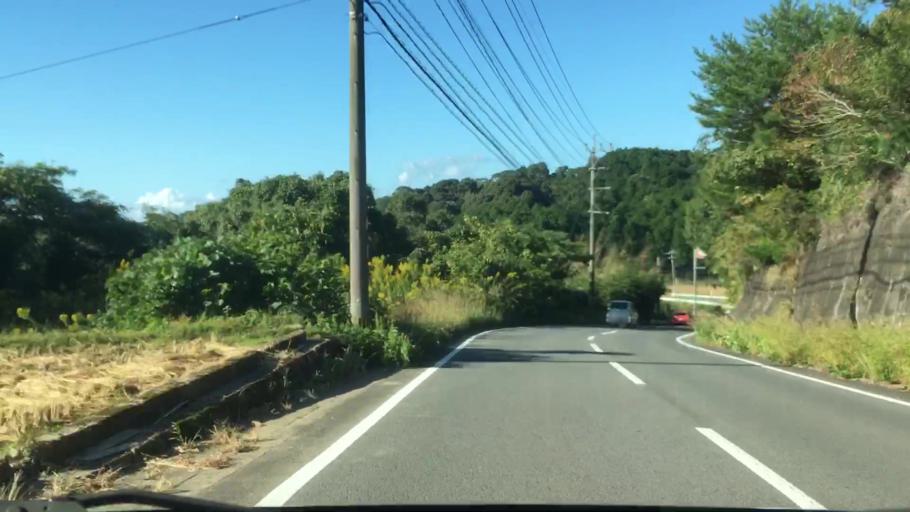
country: JP
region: Nagasaki
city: Sasebo
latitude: 32.9562
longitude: 129.6776
